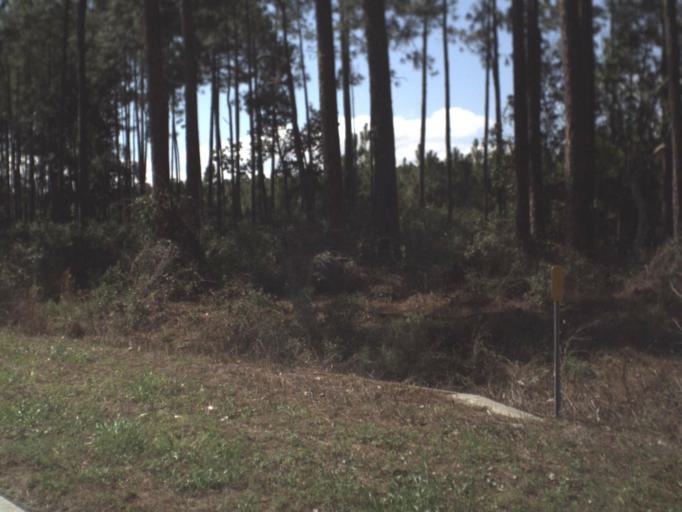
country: US
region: Florida
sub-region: Franklin County
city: Carrabelle
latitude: 29.8953
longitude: -84.5632
